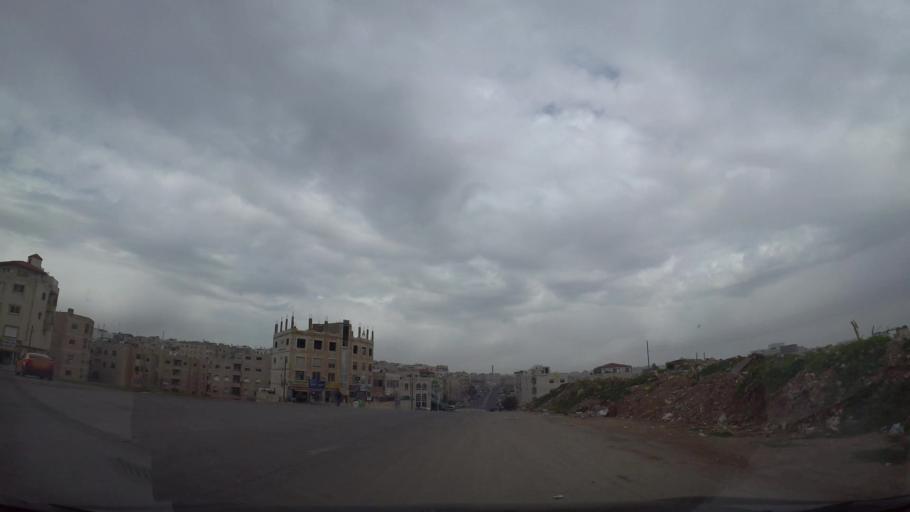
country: JO
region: Amman
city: Amman
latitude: 31.9773
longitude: 35.9302
